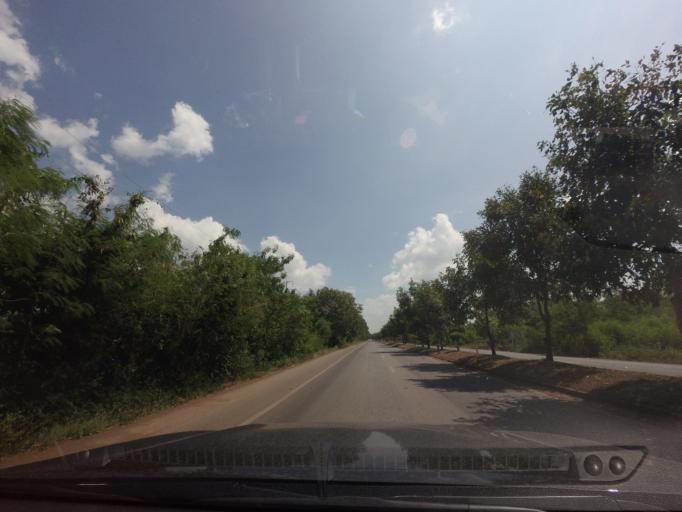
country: TH
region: Phetchabun
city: Nong Phai
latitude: 16.0541
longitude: 101.0770
